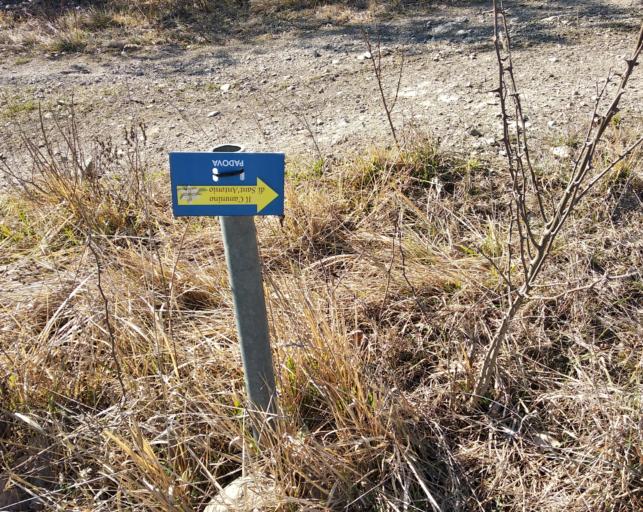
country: IT
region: Emilia-Romagna
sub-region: Provincia di Bologna
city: Pizzano
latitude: 44.3755
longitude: 11.4666
